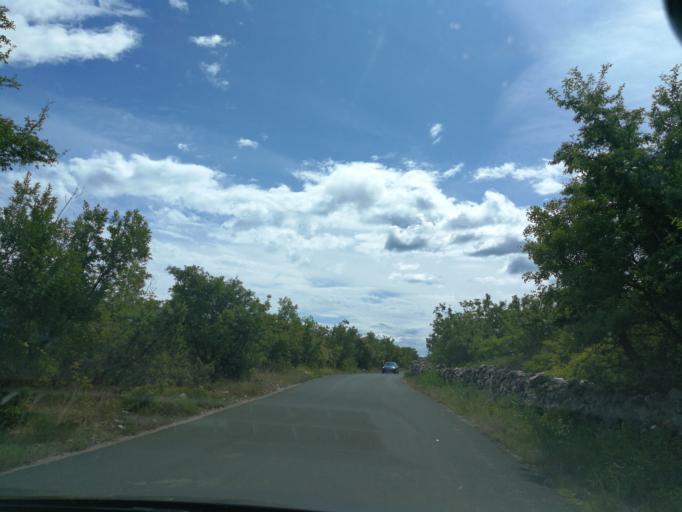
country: HR
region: Primorsko-Goranska
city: Omisalj
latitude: 45.1890
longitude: 14.5856
